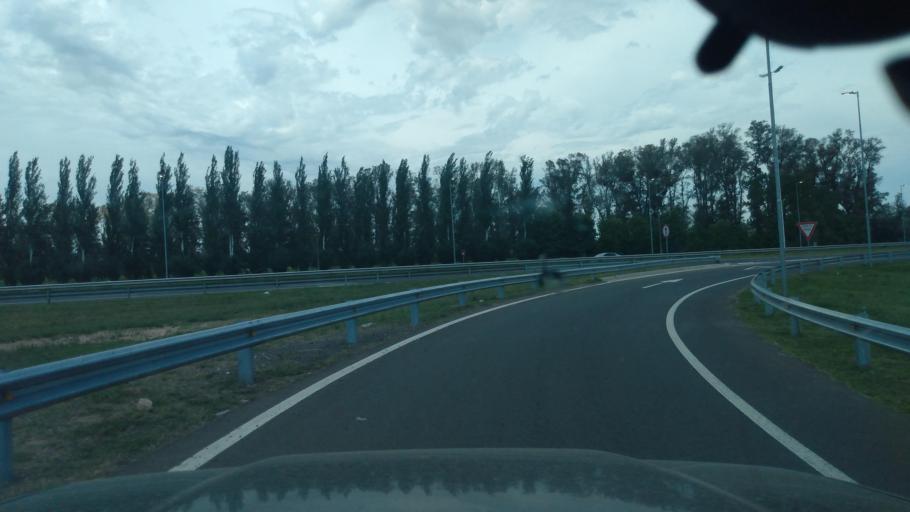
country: AR
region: Buenos Aires
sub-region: Partido de Lujan
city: Lujan
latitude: -34.5685
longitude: -59.0582
